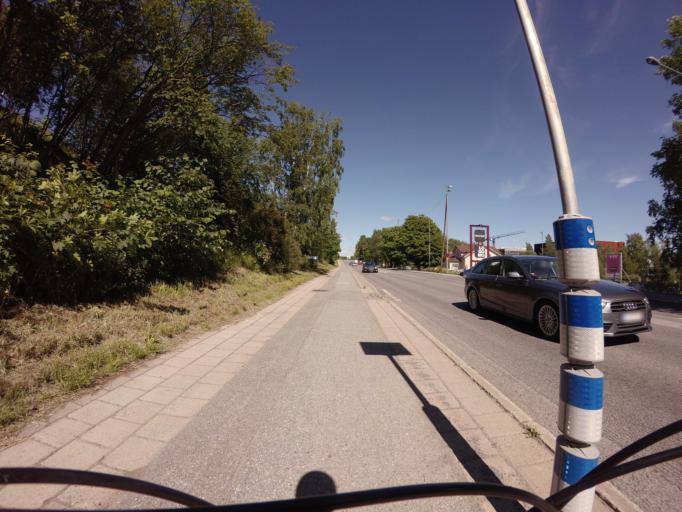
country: FI
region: Varsinais-Suomi
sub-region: Turku
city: Turku
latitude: 60.4574
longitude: 22.2544
